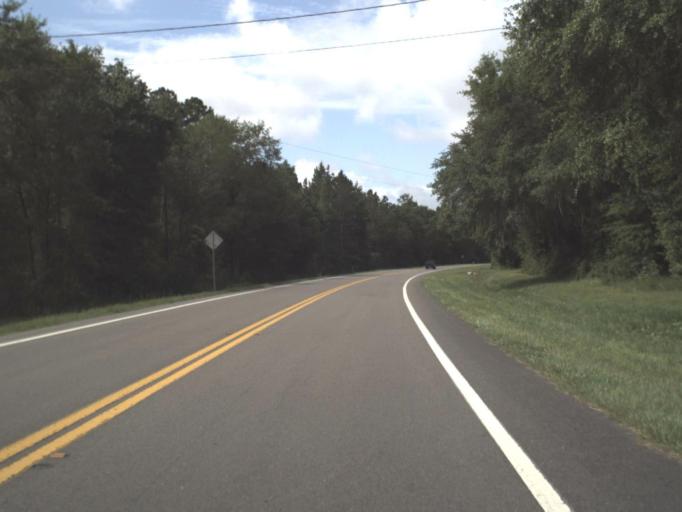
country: US
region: Florida
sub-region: Columbia County
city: Five Points
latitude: 30.3560
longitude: -82.6177
